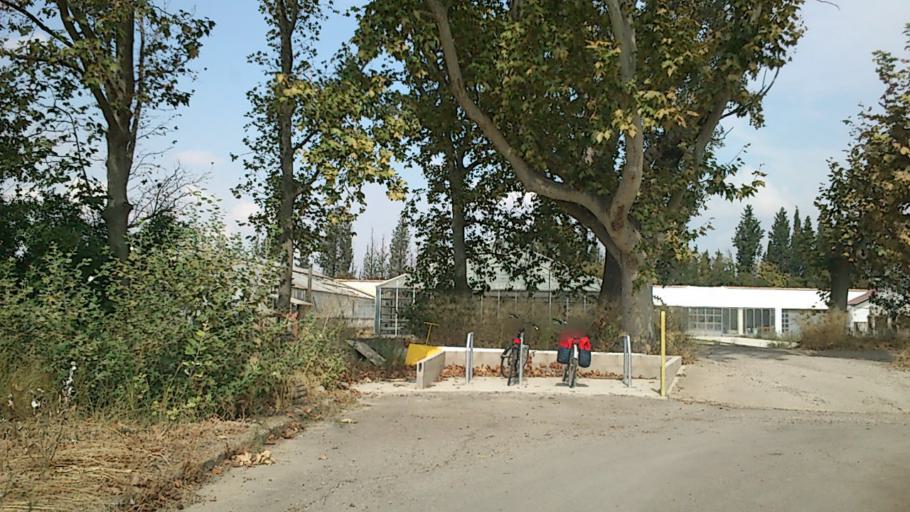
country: ES
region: Aragon
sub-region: Provincia de Zaragoza
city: Villanueva de Gallego
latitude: 41.7247
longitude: -0.8125
